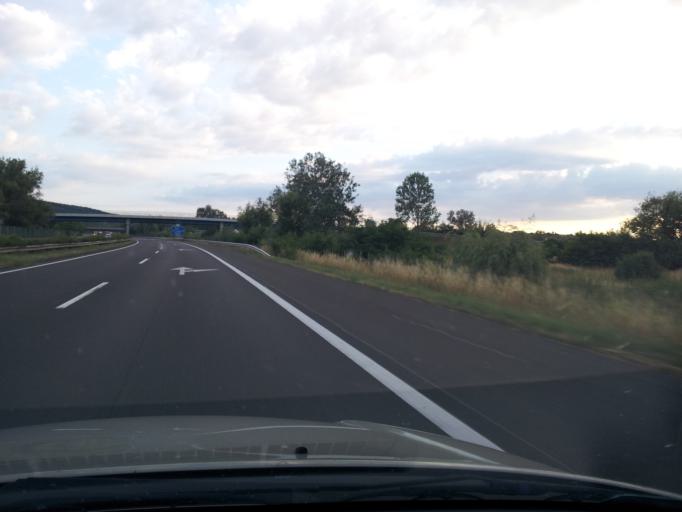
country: HU
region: Pest
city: Bag
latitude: 47.6392
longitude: 19.4830
